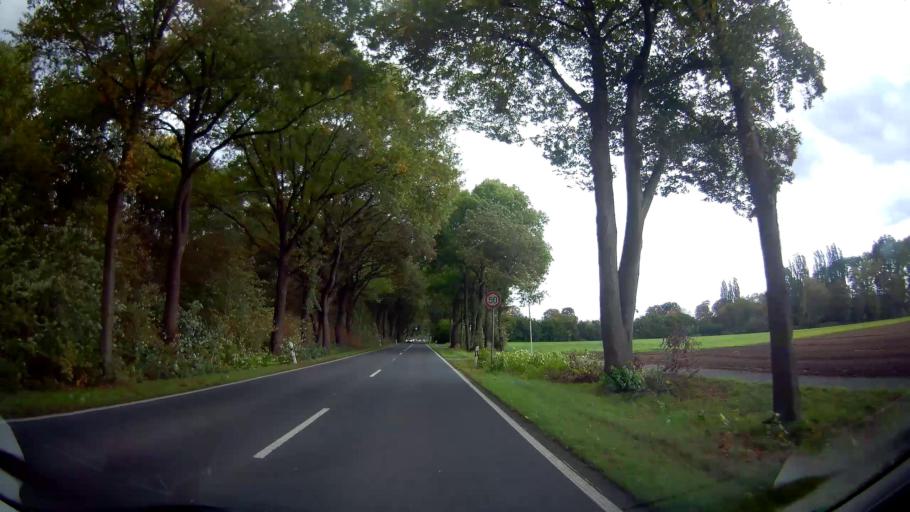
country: DE
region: North Rhine-Westphalia
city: Herten
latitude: 51.5901
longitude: 7.0867
